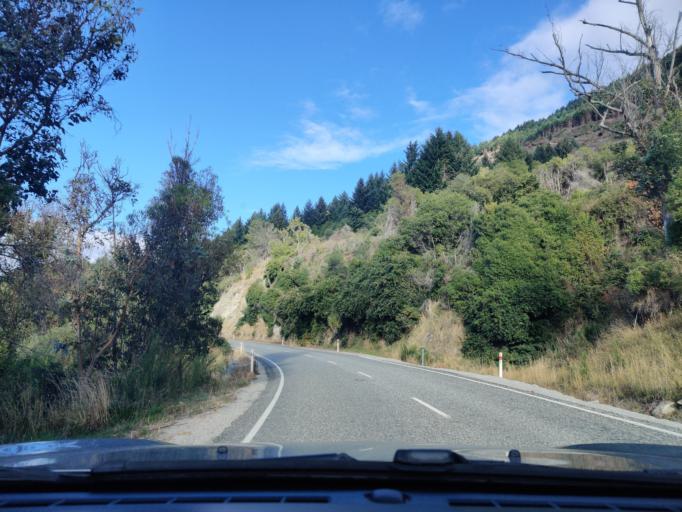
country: NZ
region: Otago
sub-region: Queenstown-Lakes District
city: Queenstown
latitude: -45.0474
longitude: 168.6231
